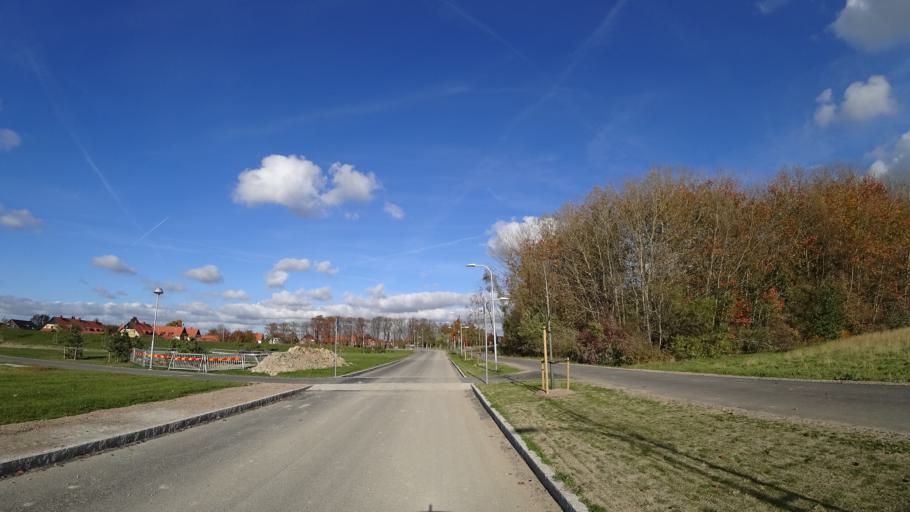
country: SE
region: Skane
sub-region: Staffanstorps Kommun
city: Staffanstorp
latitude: 55.6322
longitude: 13.2097
